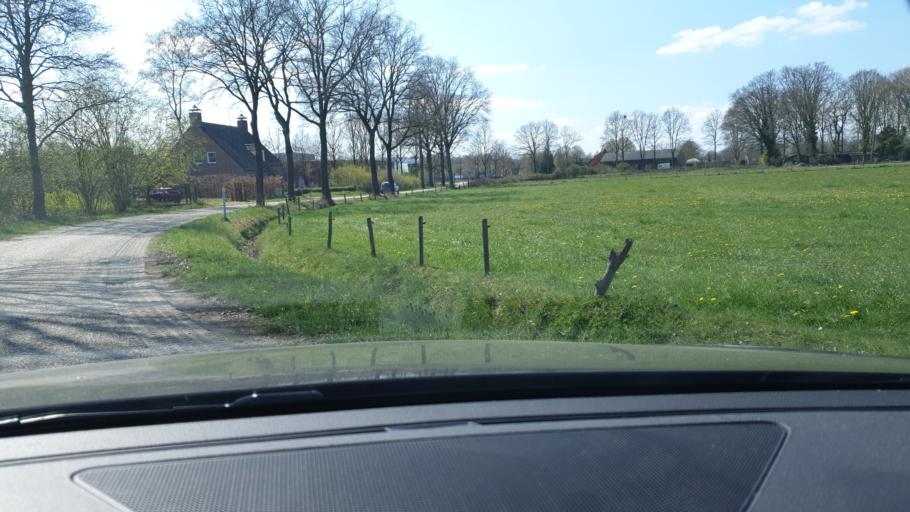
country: NL
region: North Brabant
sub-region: Gemeente Bladel en Netersel
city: Bladel
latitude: 51.3743
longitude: 5.2362
